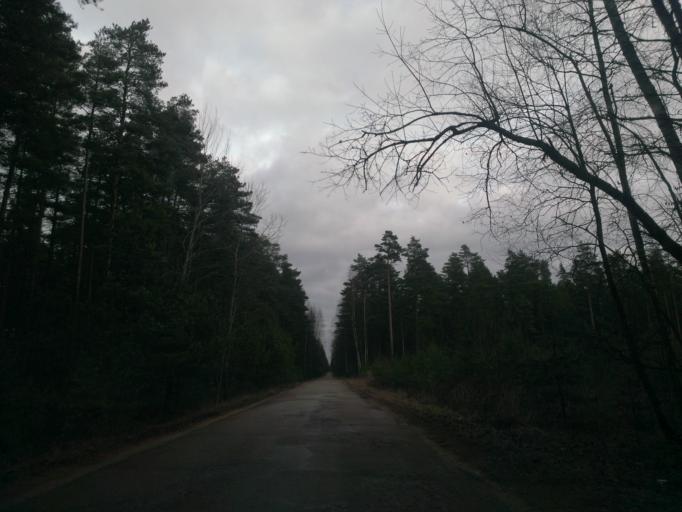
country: LV
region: Riga
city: Bergi
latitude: 57.0037
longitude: 24.3112
